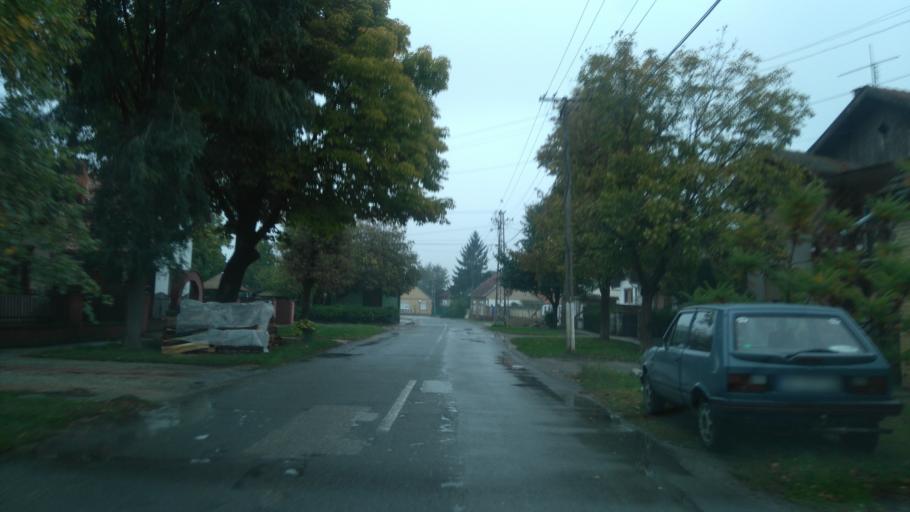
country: RS
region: Autonomna Pokrajina Vojvodina
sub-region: Juznobacki Okrug
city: Becej
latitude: 45.6185
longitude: 20.0592
